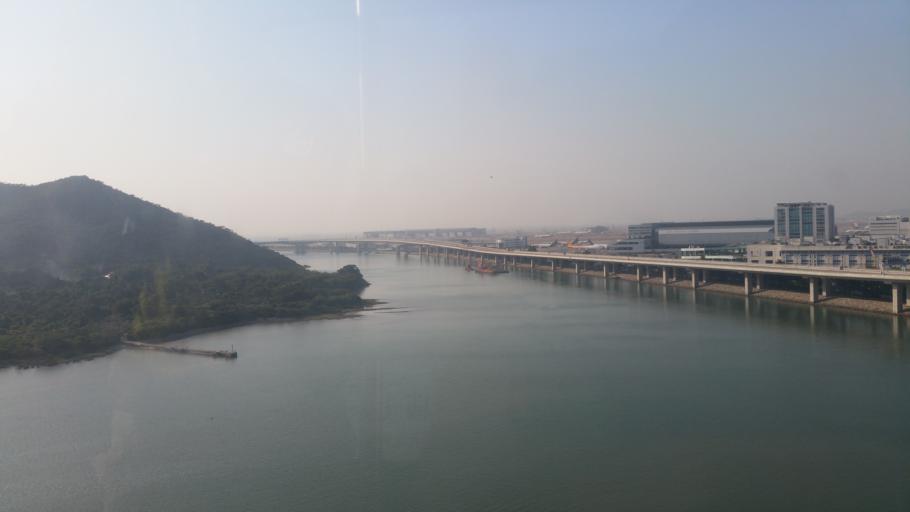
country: HK
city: Tai O
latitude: 22.2883
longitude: 113.9286
